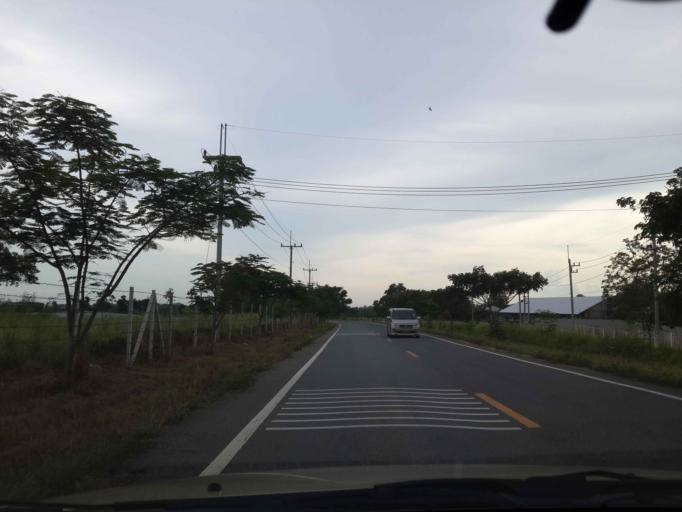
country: TH
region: Chon Buri
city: Phatthaya
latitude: 12.9163
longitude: 100.9989
